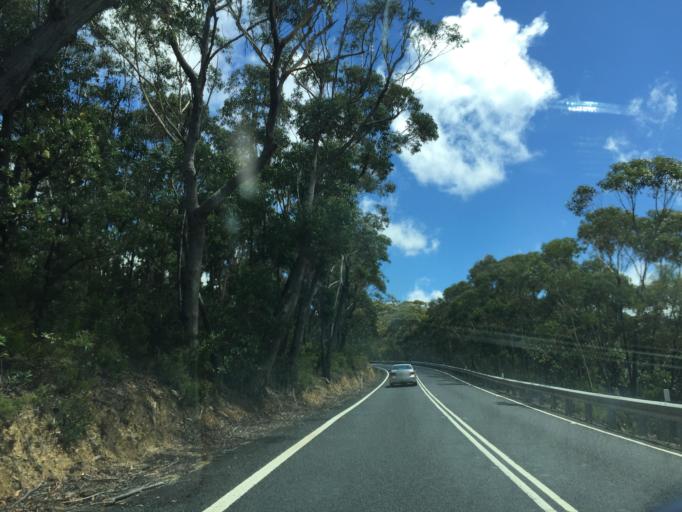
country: AU
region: New South Wales
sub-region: Blue Mountains Municipality
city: Blackheath
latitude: -33.5607
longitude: 150.3722
